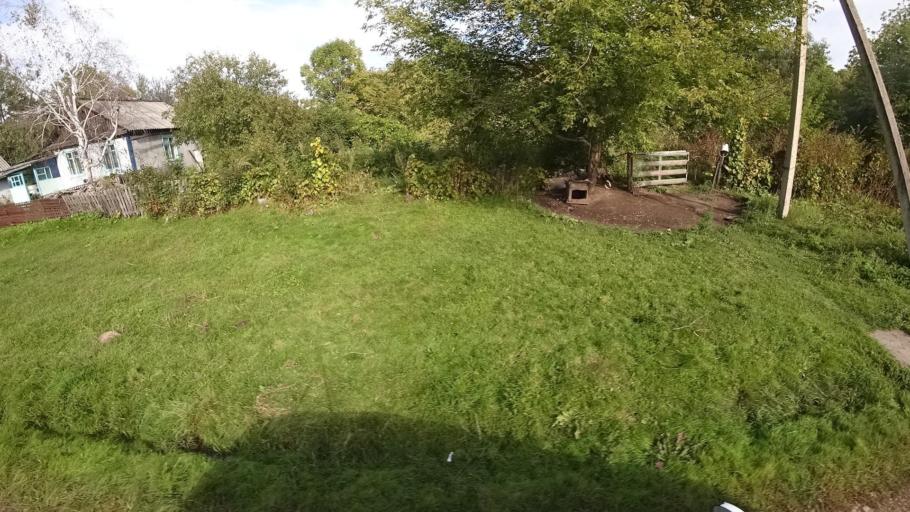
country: RU
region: Primorskiy
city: Dostoyevka
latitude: 44.2924
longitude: 133.4487
